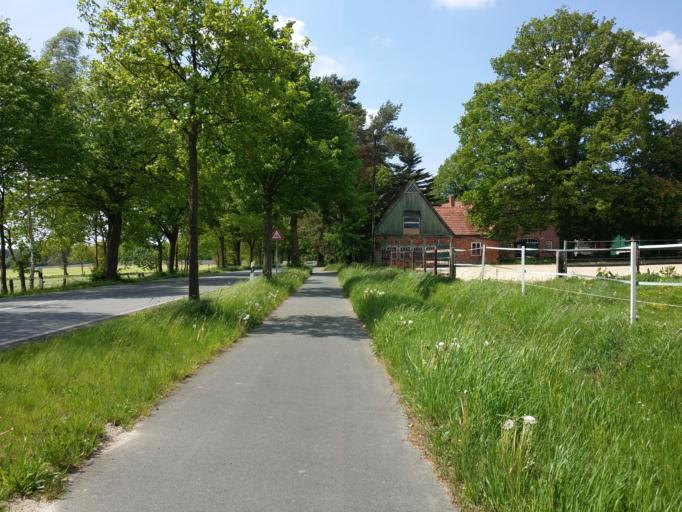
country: DE
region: Lower Saxony
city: Lubberstedt
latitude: 53.2989
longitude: 8.7696
